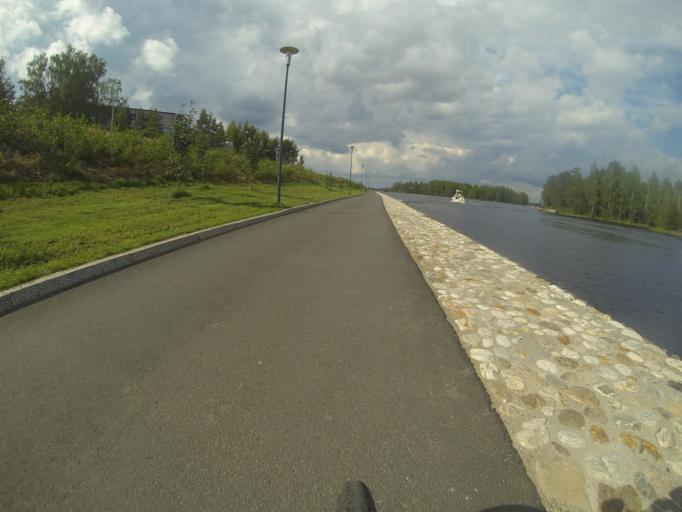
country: FI
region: Southern Savonia
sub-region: Savonlinna
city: Savonlinna
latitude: 61.8716
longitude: 28.8825
